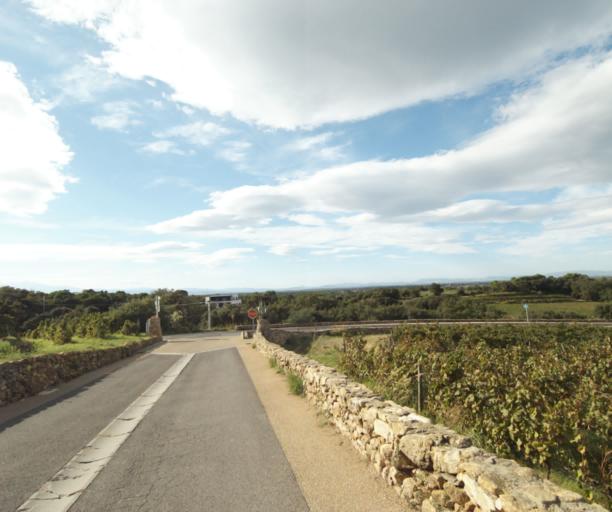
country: FR
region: Languedoc-Roussillon
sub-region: Departement des Pyrenees-Orientales
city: Argelers
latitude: 42.5328
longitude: 3.0287
